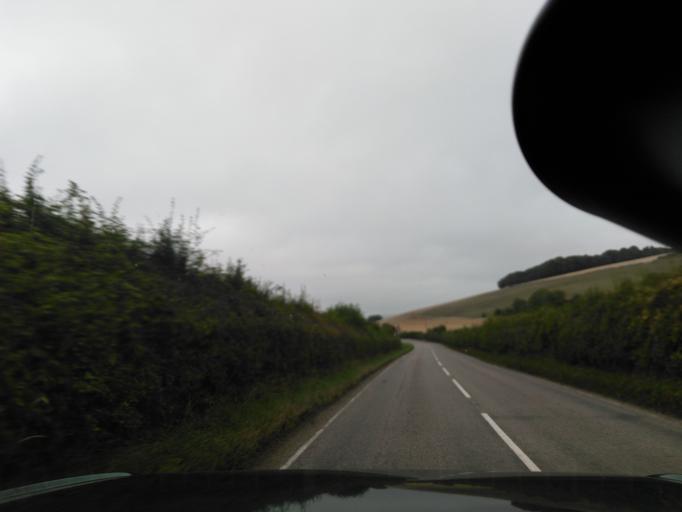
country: GB
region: England
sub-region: Dorset
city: Blandford Forum
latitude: 50.9145
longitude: -2.1955
